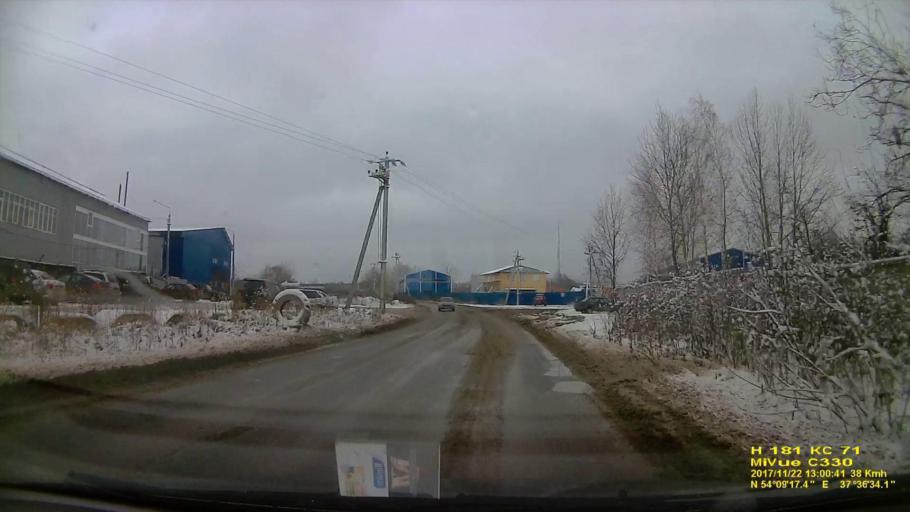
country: RU
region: Tula
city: Mendeleyevskiy
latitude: 54.1548
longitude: 37.6094
